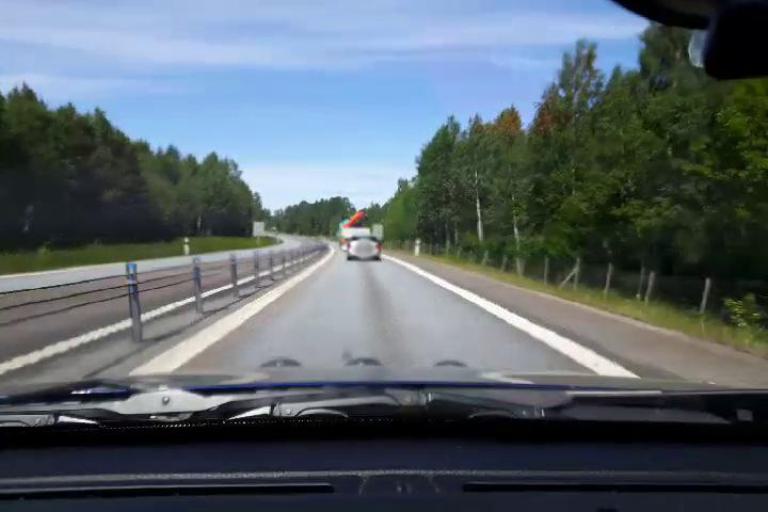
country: SE
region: Gaevleborg
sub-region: Gavle Kommun
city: Norrsundet
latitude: 60.9500
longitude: 17.0311
